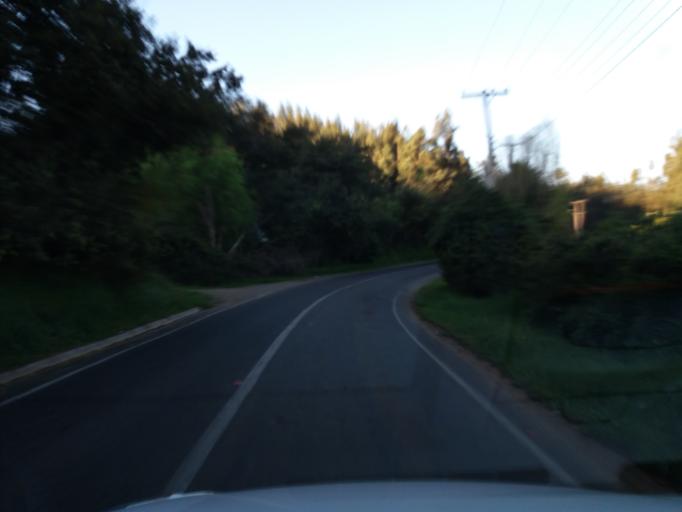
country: CL
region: Valparaiso
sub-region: Provincia de Quillota
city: Quillota
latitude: -32.8872
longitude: -71.2816
